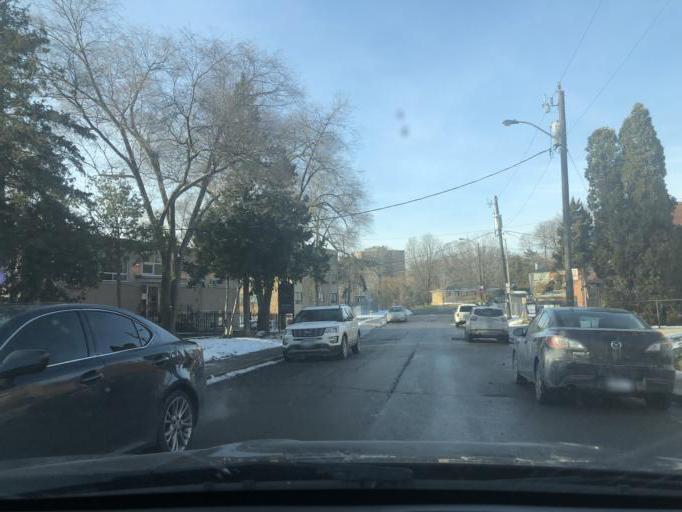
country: CA
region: Ontario
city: Toronto
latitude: 43.6928
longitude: -79.4824
